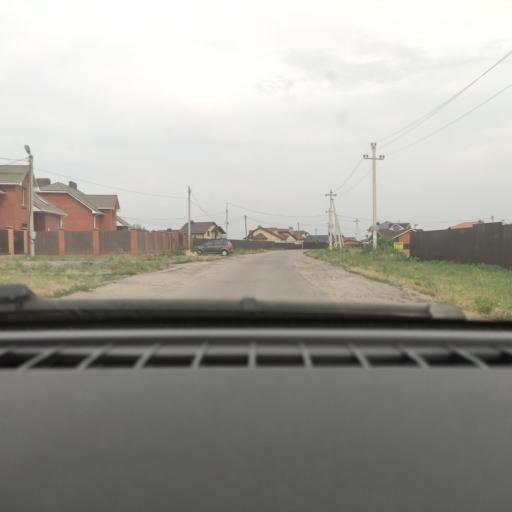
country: RU
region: Voronezj
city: Novaya Usman'
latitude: 51.6499
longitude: 39.3376
